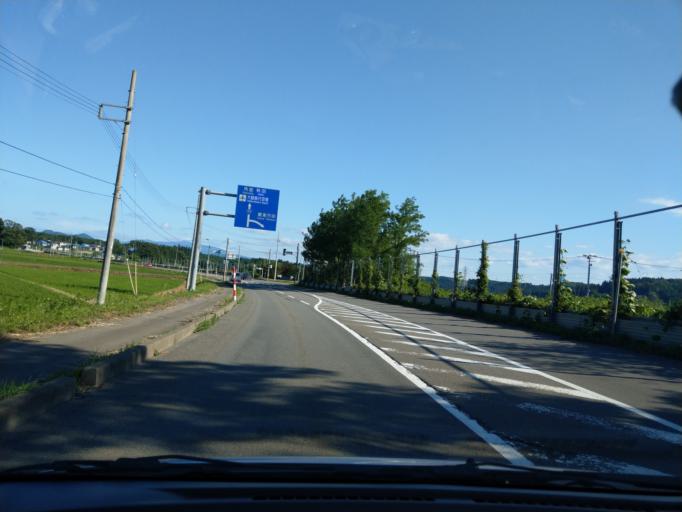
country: JP
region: Akita
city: Takanosu
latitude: 40.1962
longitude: 140.3963
